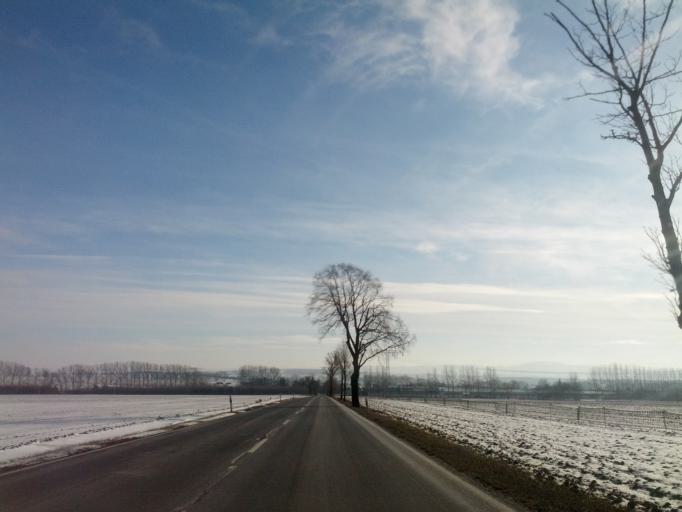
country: DE
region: Thuringia
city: Friedrichswerth
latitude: 51.0316
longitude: 10.5322
